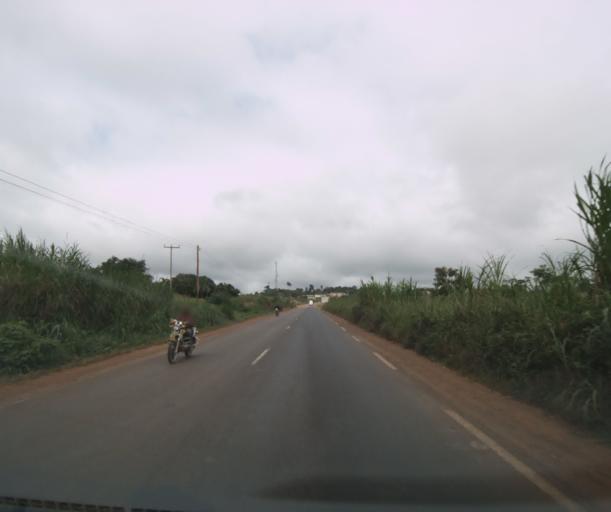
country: CM
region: Centre
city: Mbankomo
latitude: 3.7897
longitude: 11.4076
